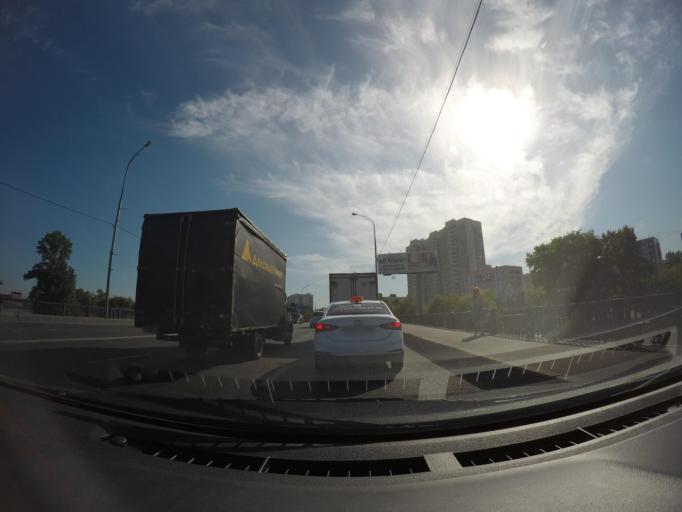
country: RU
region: Moscow
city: Mar'ina Roshcha
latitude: 55.8090
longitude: 37.6170
